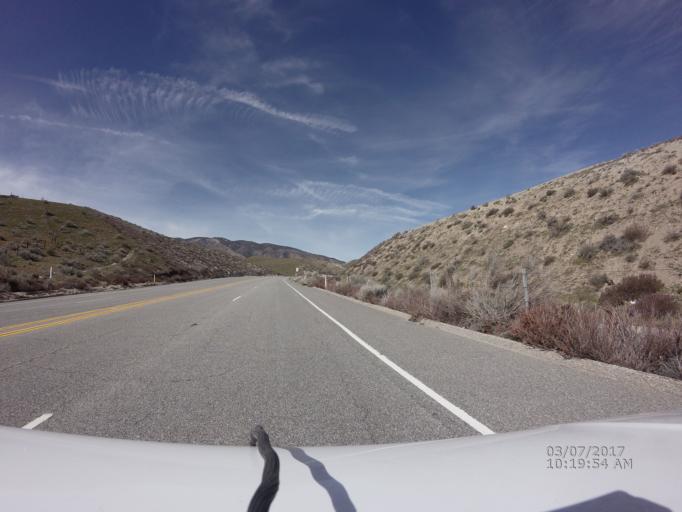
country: US
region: California
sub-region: Kern County
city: Lebec
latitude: 34.7961
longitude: -118.8713
